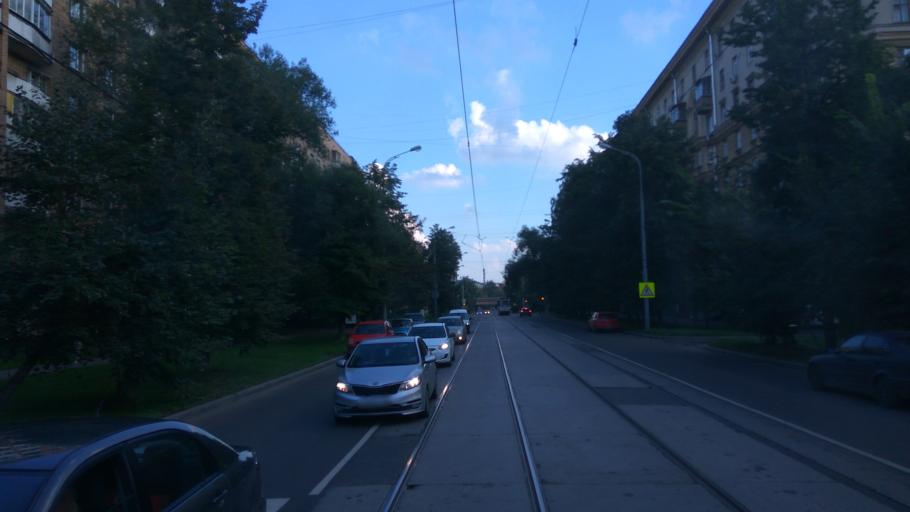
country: RU
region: Moscow
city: Likhobory
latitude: 55.8103
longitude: 37.5737
